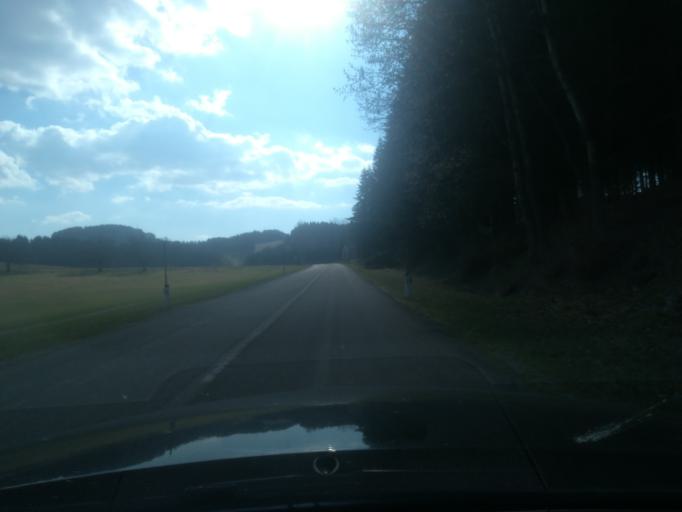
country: AT
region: Lower Austria
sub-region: Politischer Bezirk Zwettl
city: Langschlag
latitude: 48.4693
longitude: 14.7177
